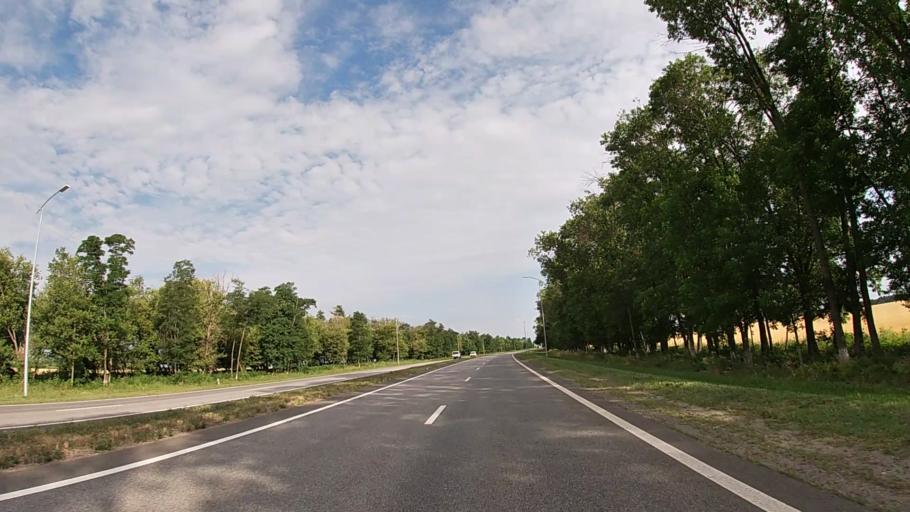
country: RU
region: Belgorod
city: Tomarovka
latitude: 50.6733
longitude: 36.2973
